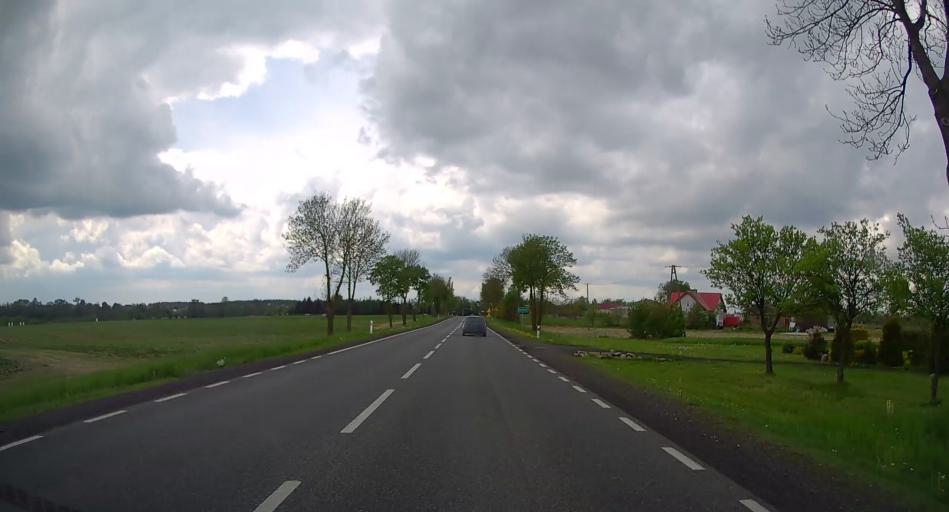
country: PL
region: Masovian Voivodeship
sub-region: Powiat plonski
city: Zaluski
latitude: 52.4354
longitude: 20.4727
